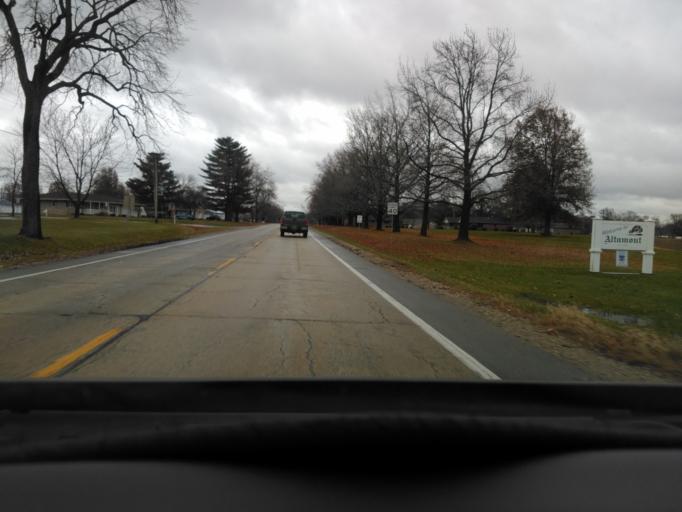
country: US
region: Illinois
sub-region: Effingham County
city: Altamont
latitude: 39.0523
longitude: -88.7572
